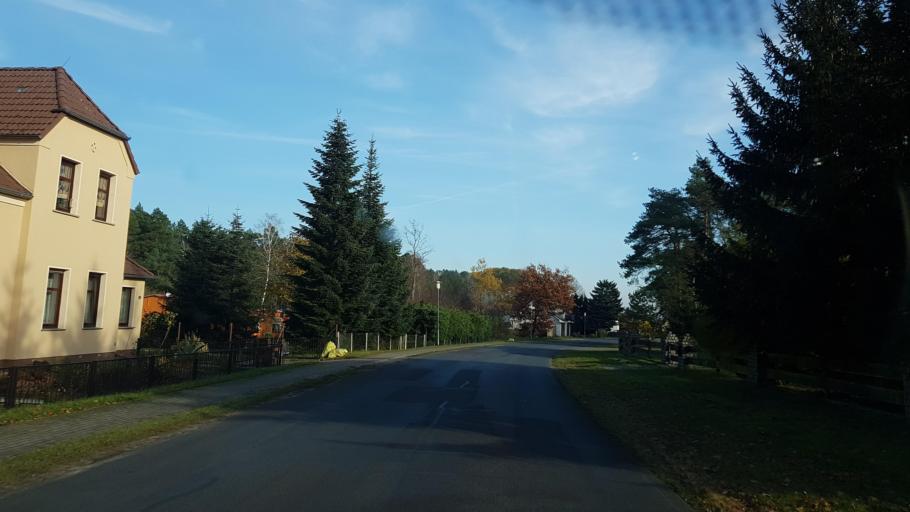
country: DE
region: Brandenburg
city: Brussow
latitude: 53.4851
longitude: 14.2287
